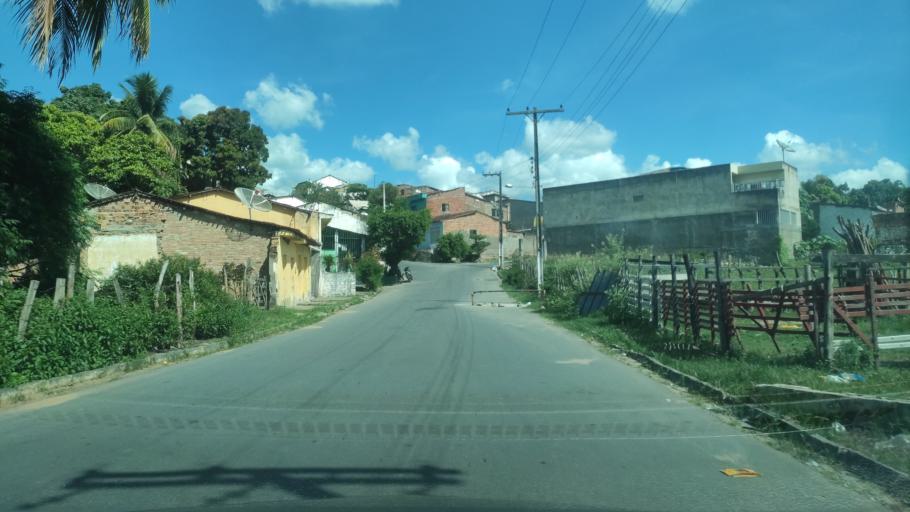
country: BR
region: Alagoas
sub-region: Uniao Dos Palmares
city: Uniao dos Palmares
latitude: -9.1569
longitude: -36.0357
